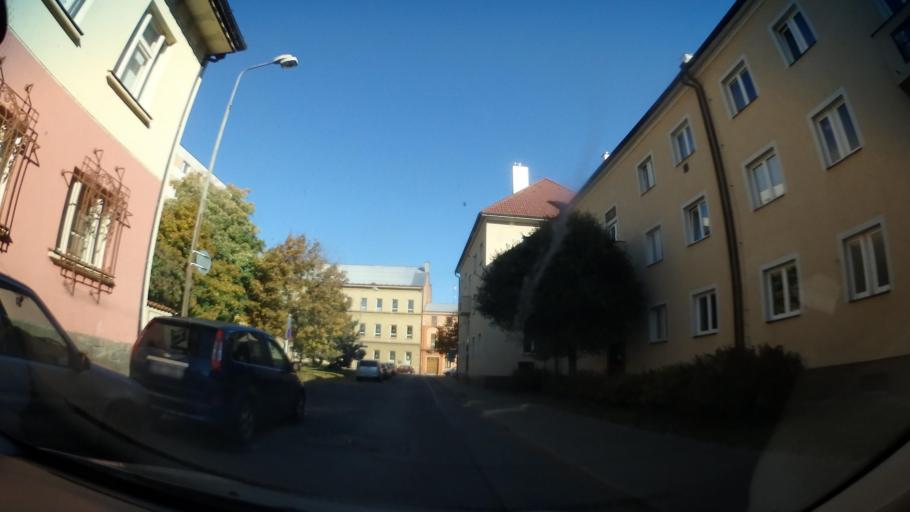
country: CZ
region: Pardubicky
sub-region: Okres Chrudim
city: Chrudim
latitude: 49.9484
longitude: 15.7914
